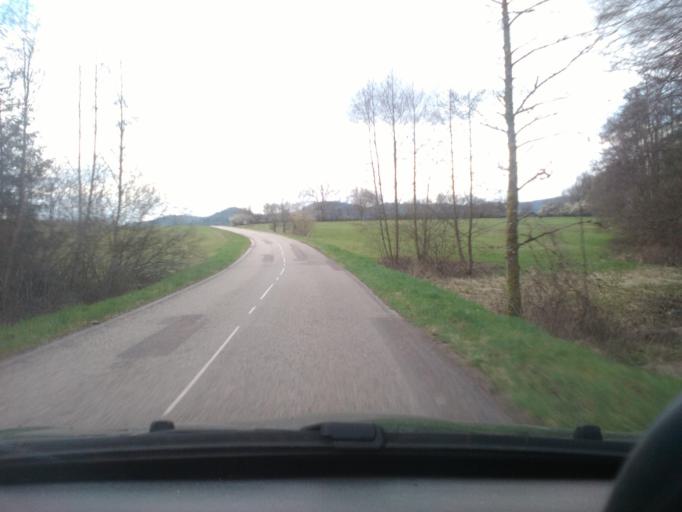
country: FR
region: Lorraine
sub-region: Departement des Vosges
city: Etival-Clairefontaine
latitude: 48.3317
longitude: 6.8233
